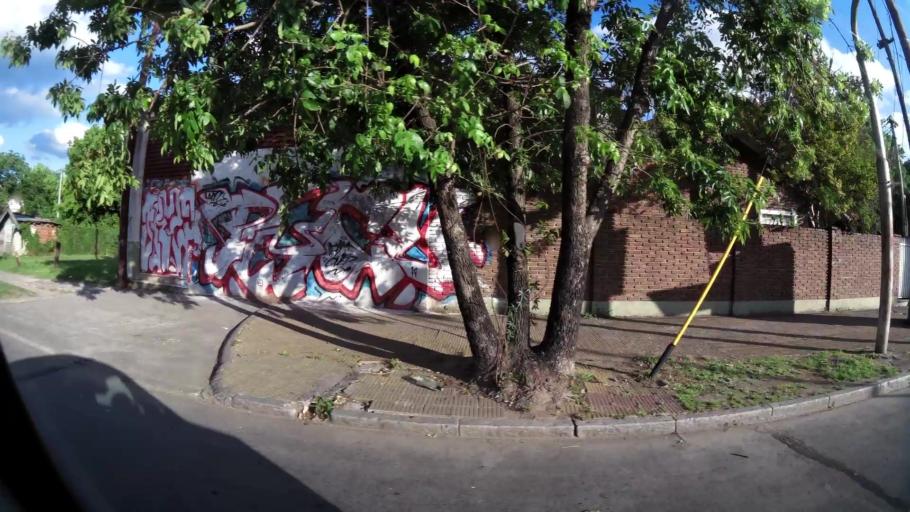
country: AR
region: Buenos Aires
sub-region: Partido de La Plata
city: La Plata
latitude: -34.8943
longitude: -57.9495
